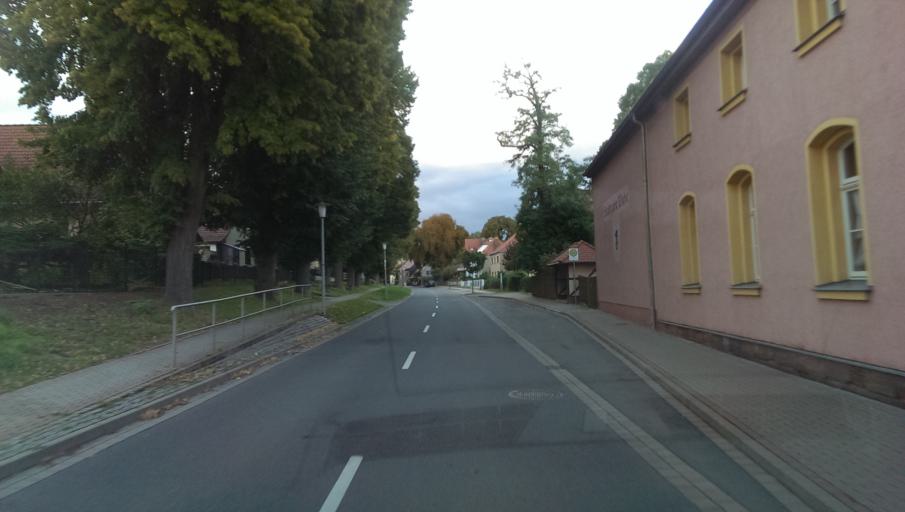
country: DE
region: Thuringia
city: Wiehe
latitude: 51.2630
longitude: 11.4210
